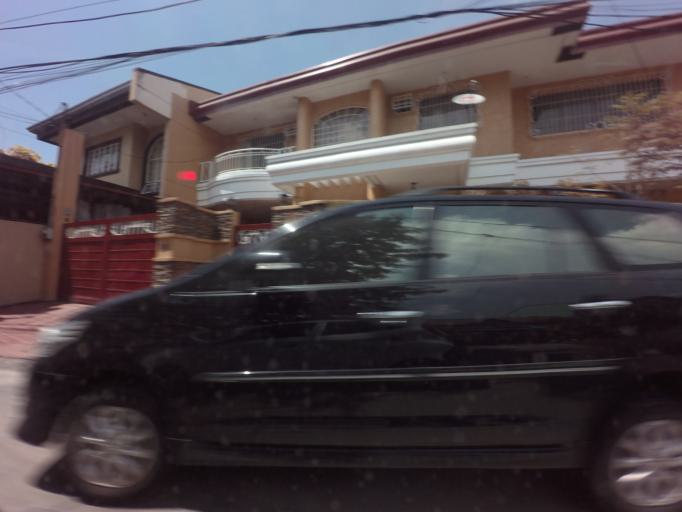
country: PH
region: Calabarzon
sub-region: Province of Rizal
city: Las Pinas
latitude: 14.4278
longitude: 120.9870
